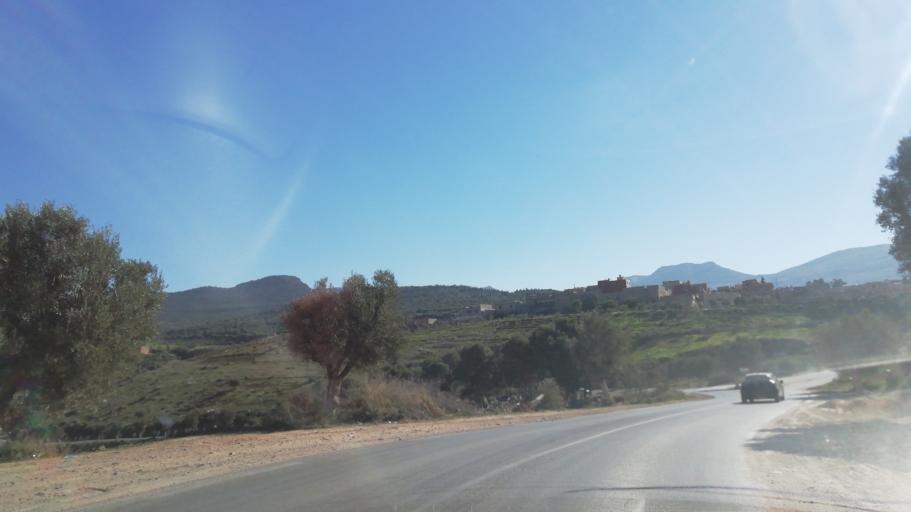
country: DZ
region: Tlemcen
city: Beni Mester
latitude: 34.8301
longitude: -1.5100
